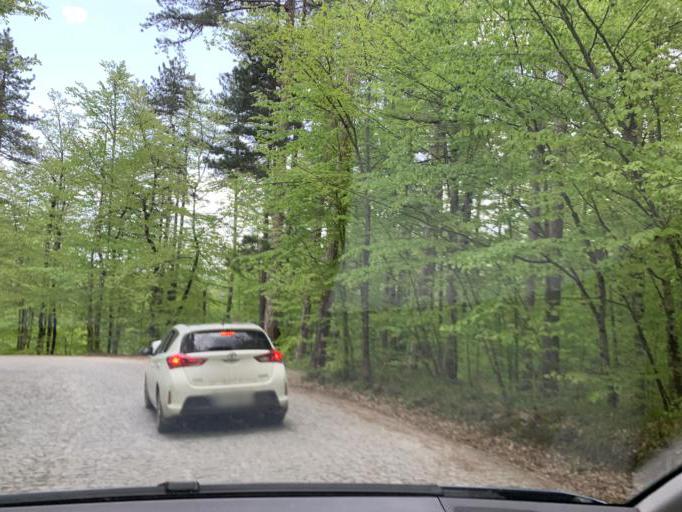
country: TR
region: Zonguldak
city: Egerci
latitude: 40.9396
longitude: 31.7439
